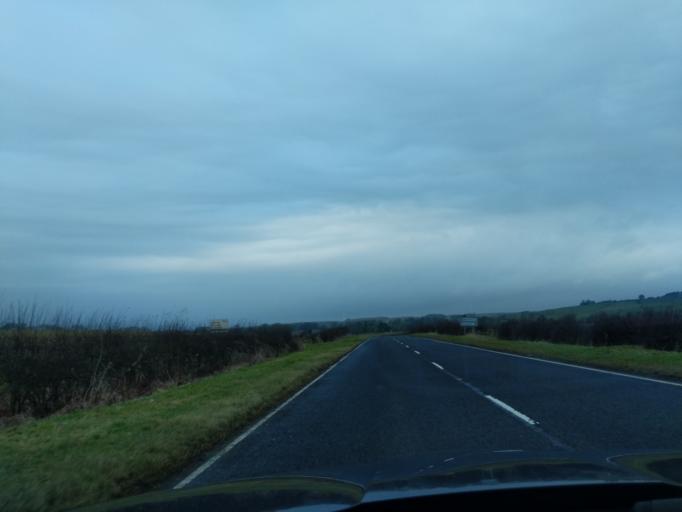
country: GB
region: England
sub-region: Northumberland
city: Rothley
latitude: 55.1477
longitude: -1.9960
